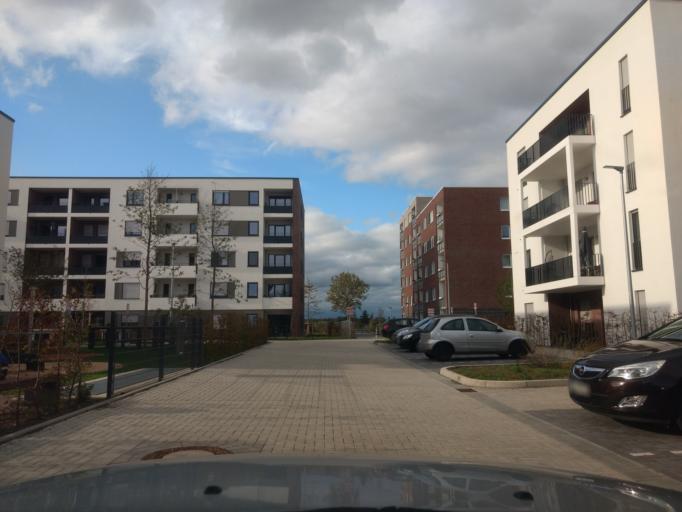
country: DE
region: North Rhine-Westphalia
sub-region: Regierungsbezirk Dusseldorf
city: Meerbusch
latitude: 51.2415
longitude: 6.7136
